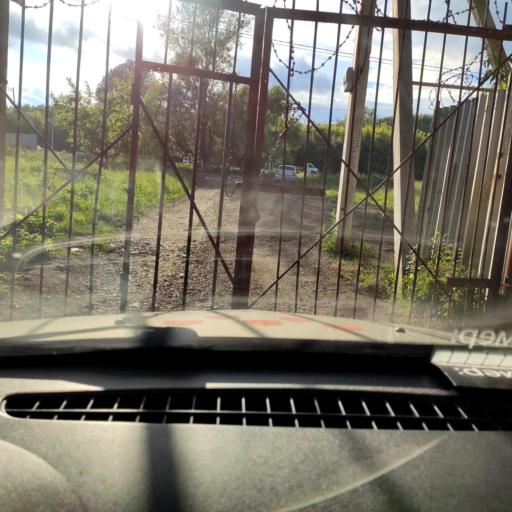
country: RU
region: Bashkortostan
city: Ufa
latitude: 54.8298
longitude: 56.1332
